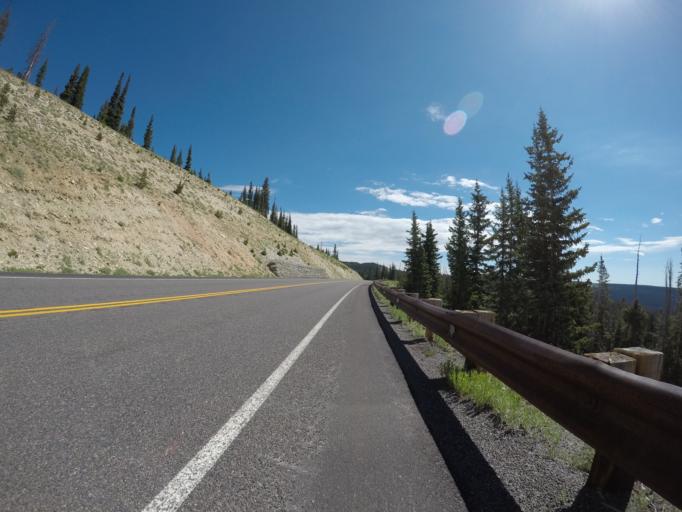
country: US
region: Wyoming
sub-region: Carbon County
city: Saratoga
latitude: 41.3164
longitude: -106.3483
